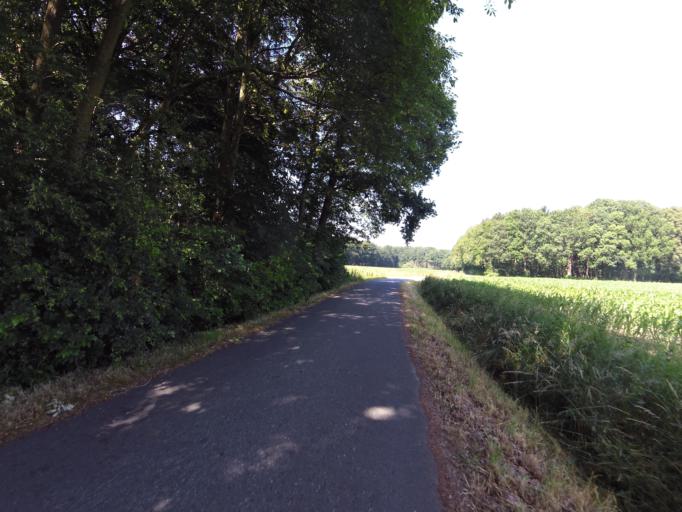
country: BE
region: Flanders
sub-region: Provincie West-Vlaanderen
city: Zedelgem
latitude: 51.1560
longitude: 3.1413
